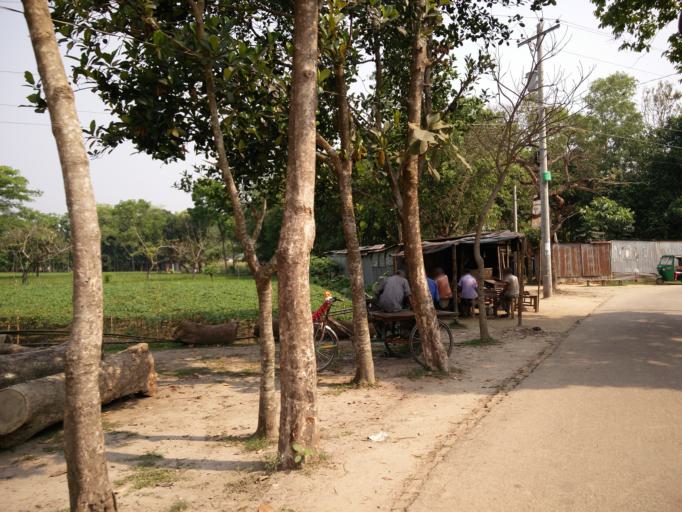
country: BD
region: Dhaka
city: Muktagacha
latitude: 24.9267
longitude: 90.2478
